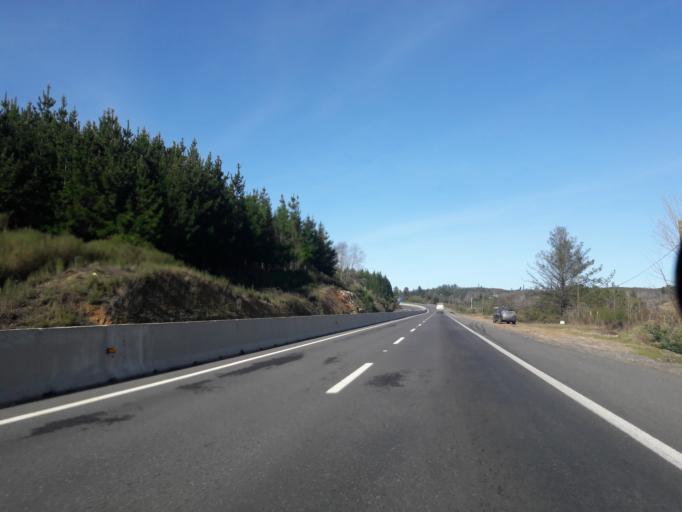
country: CL
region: Biobio
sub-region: Provincia de Concepcion
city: Chiguayante
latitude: -36.9202
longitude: -72.7739
